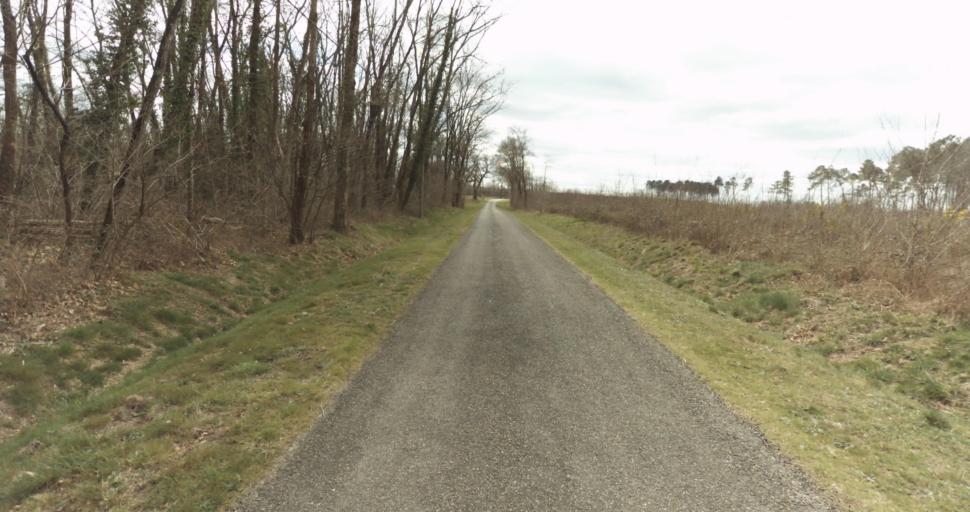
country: FR
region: Aquitaine
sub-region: Departement des Landes
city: Roquefort
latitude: 44.0674
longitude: -0.3980
